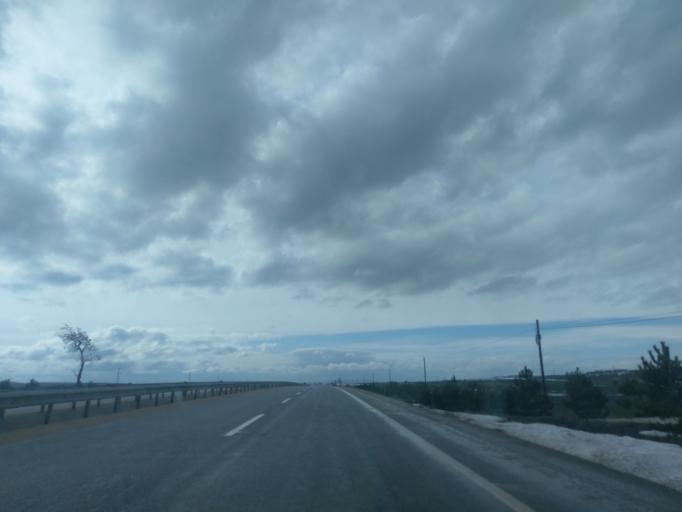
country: TR
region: Eskisehir
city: Inonu
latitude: 39.7238
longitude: 30.2677
